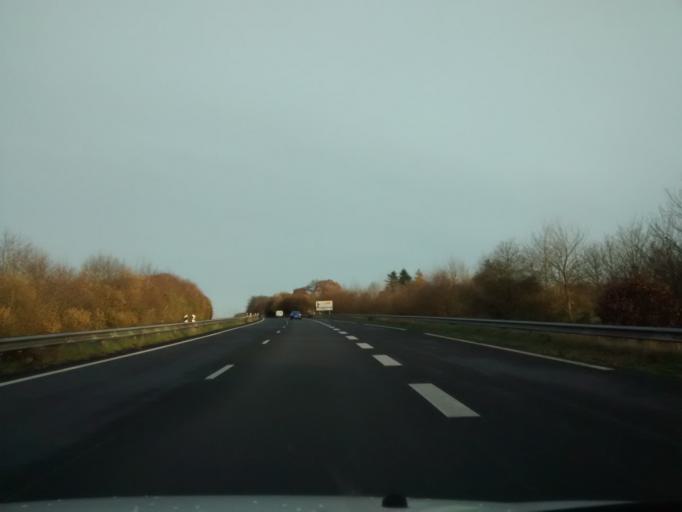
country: FR
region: Brittany
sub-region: Departement d'Ille-et-Vilaine
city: Pleugueneuc
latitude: 48.4101
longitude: -1.9074
